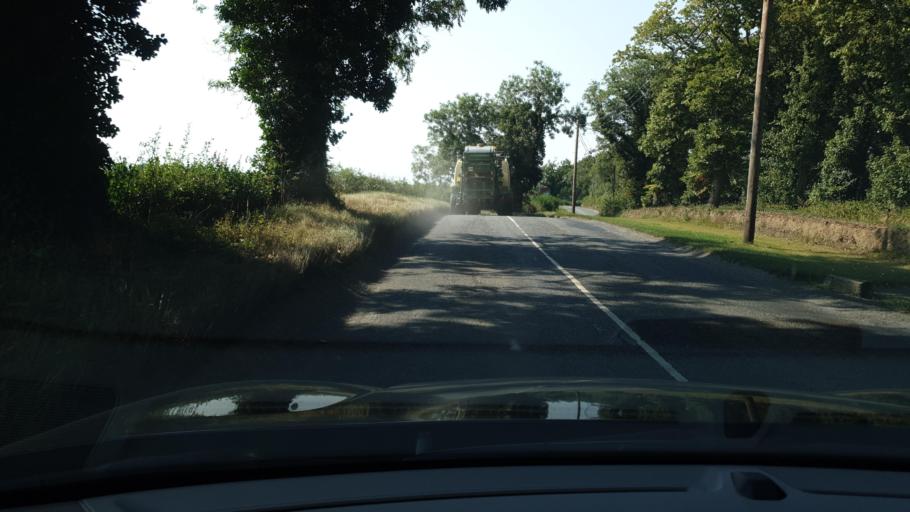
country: IE
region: Leinster
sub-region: An Mhi
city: Athboy
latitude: 53.6151
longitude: -6.9028
